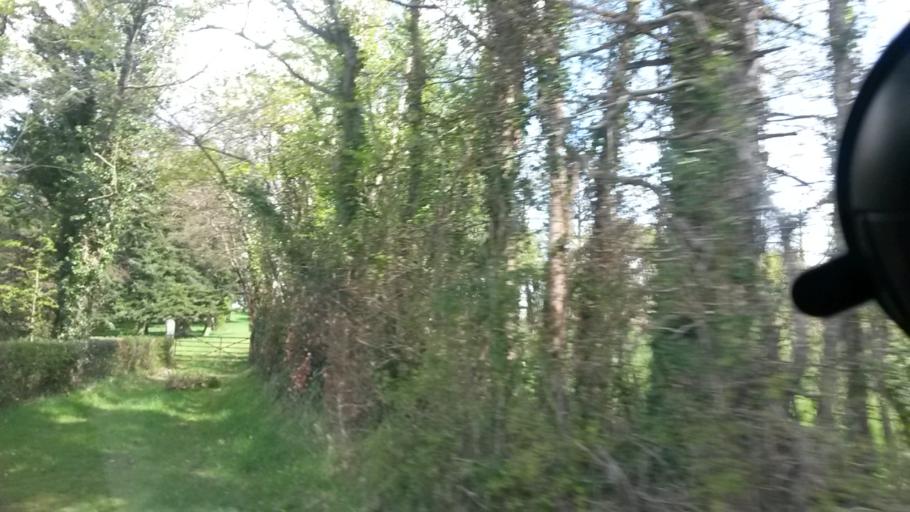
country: GB
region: Northern Ireland
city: Lisnaskea
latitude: 54.1858
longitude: -7.4882
